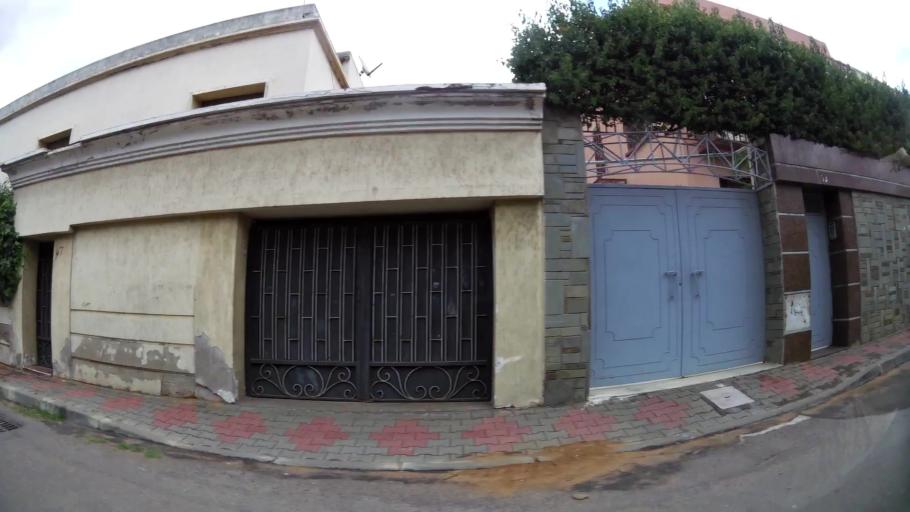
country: MA
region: Grand Casablanca
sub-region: Casablanca
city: Casablanca
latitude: 33.5610
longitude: -7.6111
